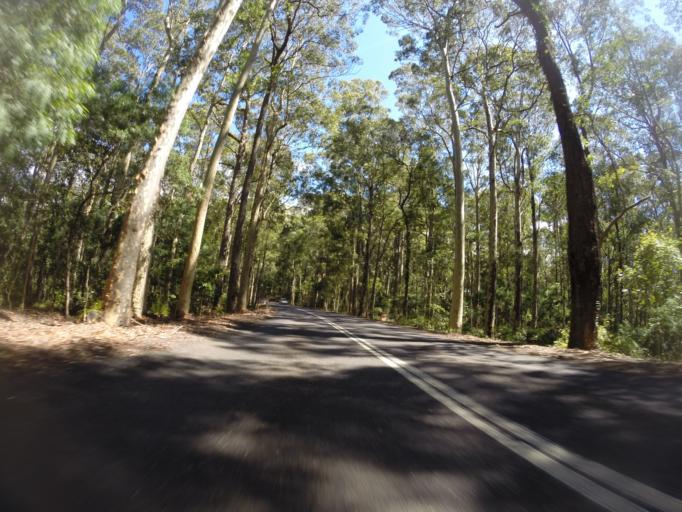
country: AU
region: New South Wales
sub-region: Eurobodalla
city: Batemans Bay
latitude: -35.6602
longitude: 150.2562
